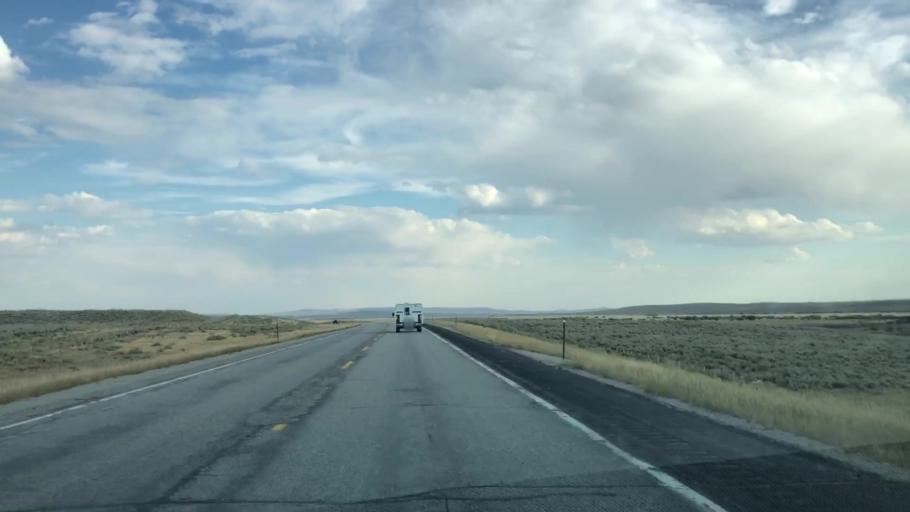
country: US
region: Wyoming
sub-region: Sublette County
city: Pinedale
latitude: 43.0497
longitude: -110.1505
